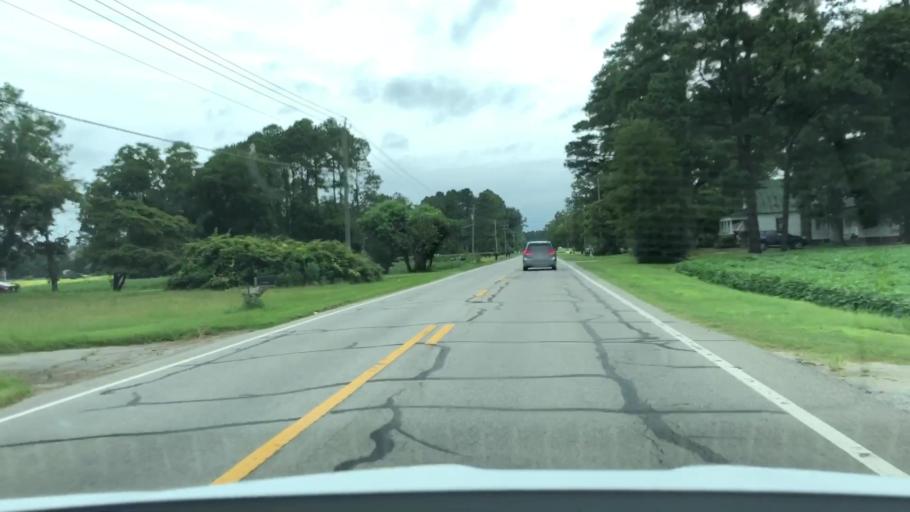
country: US
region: North Carolina
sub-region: Lenoir County
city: Kinston
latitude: 35.2111
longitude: -77.5683
